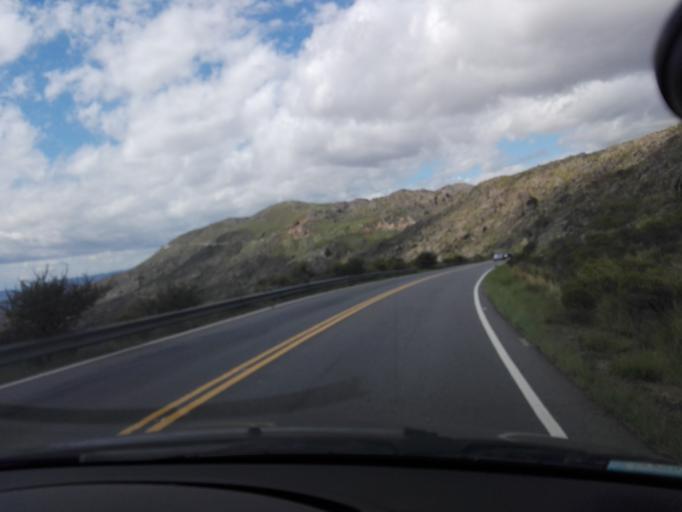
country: AR
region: Cordoba
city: Mina Clavero
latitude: -31.7880
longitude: -64.9127
